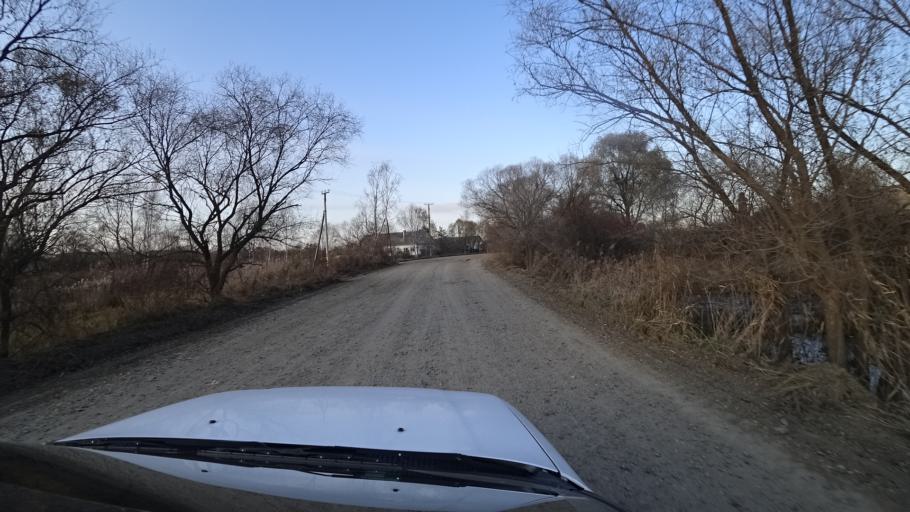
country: RU
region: Primorskiy
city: Dal'nerechensk
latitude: 45.9399
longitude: 133.8212
